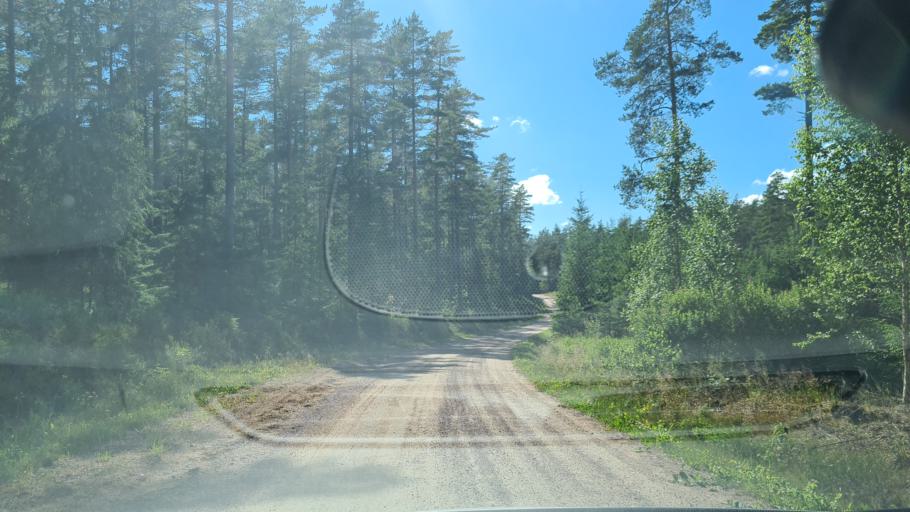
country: SE
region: OEstergoetland
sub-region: Norrkopings Kommun
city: Krokek
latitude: 58.6933
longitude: 16.4275
